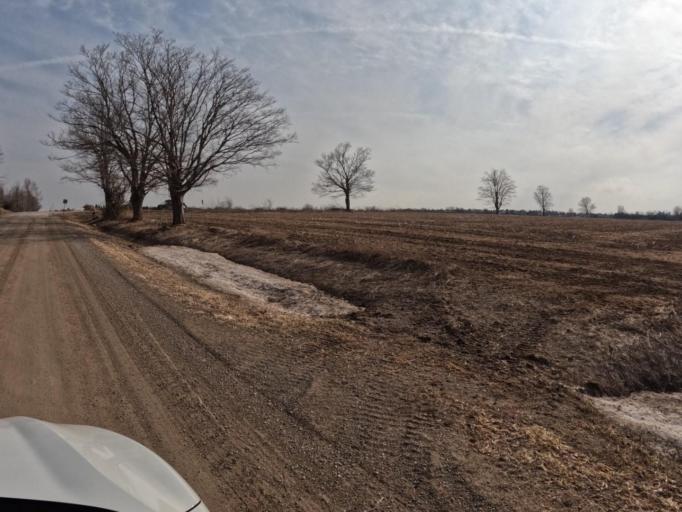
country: CA
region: Ontario
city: Orangeville
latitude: 43.8958
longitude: -80.2668
